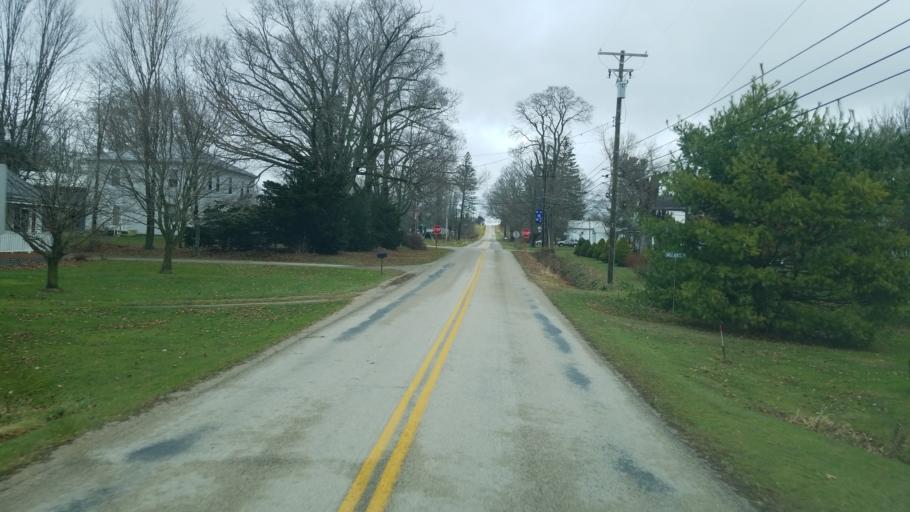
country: US
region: Ohio
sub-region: Ashtabula County
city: North Kingsville
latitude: 41.8572
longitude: -80.6175
